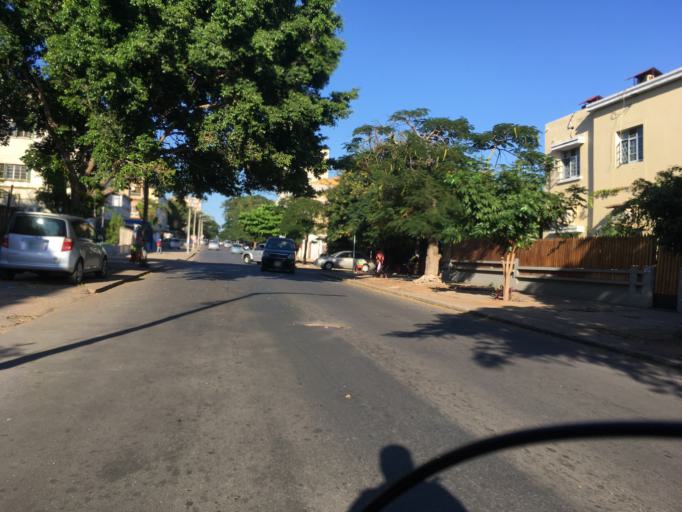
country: MZ
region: Maputo City
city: Maputo
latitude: -25.9611
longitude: 32.5799
